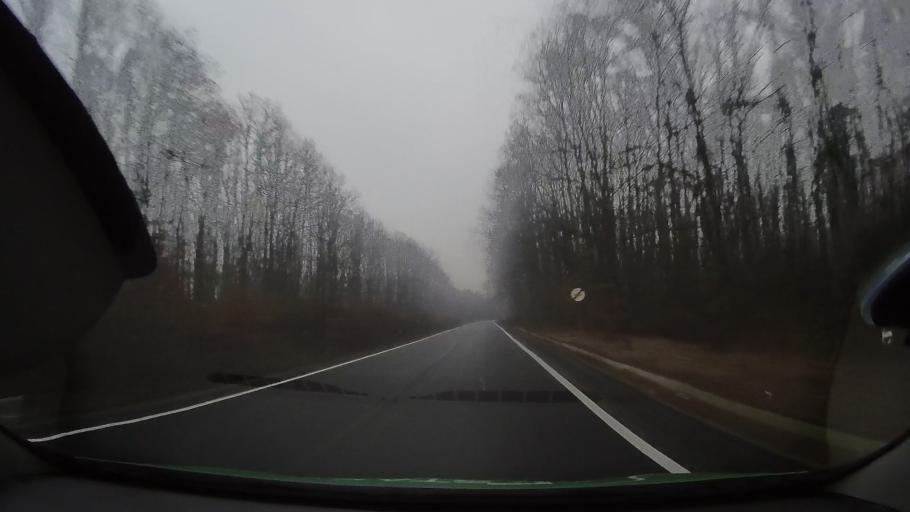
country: RO
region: Bihor
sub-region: Comuna Olcea
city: Olcea
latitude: 46.7014
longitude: 21.9639
